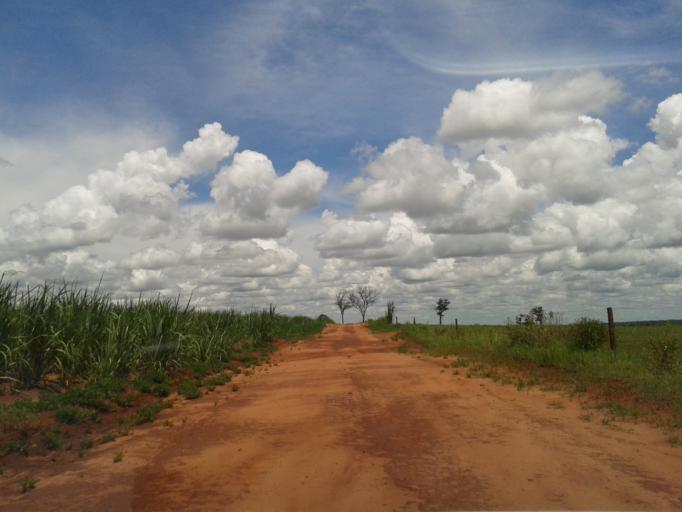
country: BR
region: Minas Gerais
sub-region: Santa Vitoria
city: Santa Vitoria
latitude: -19.2017
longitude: -50.6561
